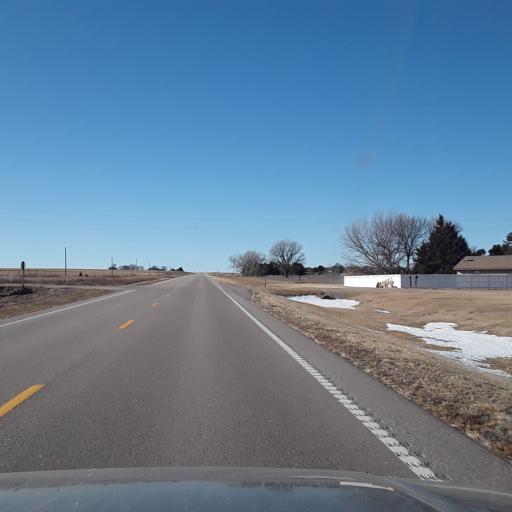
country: US
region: Nebraska
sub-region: Frontier County
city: Stockville
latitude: 40.7003
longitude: -100.2651
